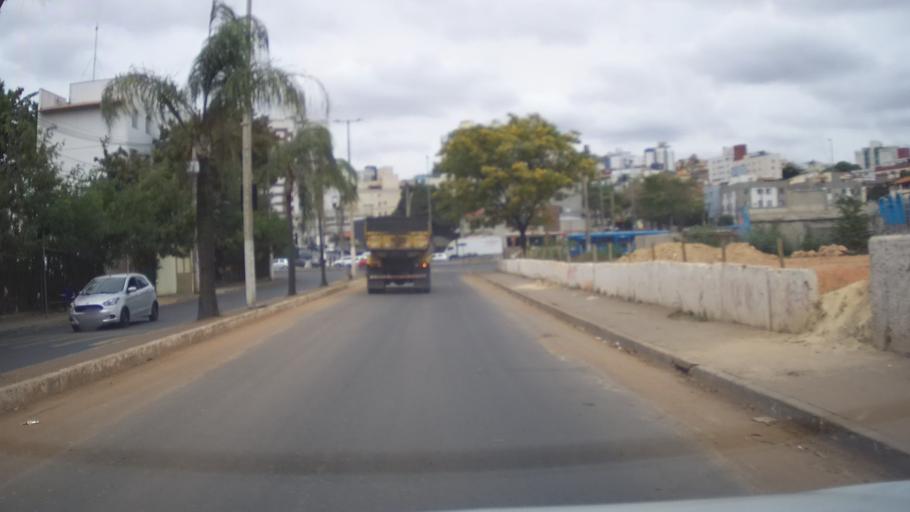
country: BR
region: Minas Gerais
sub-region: Belo Horizonte
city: Belo Horizonte
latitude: -19.8695
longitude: -43.9272
